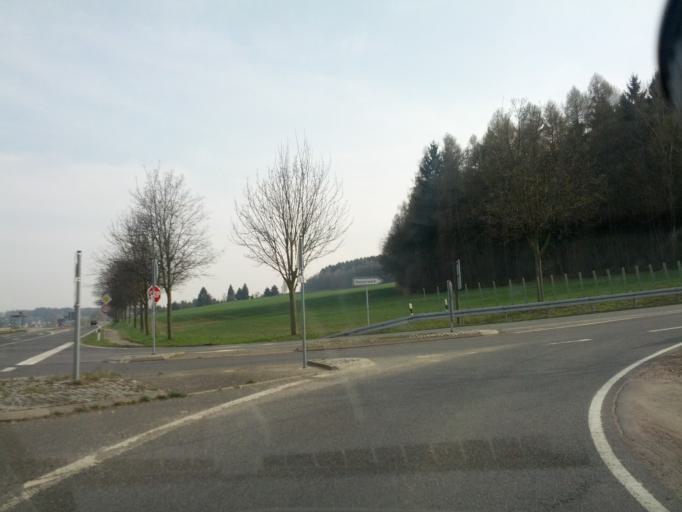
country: DE
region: Saxony
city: Kirchberg
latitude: 50.6269
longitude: 12.5716
